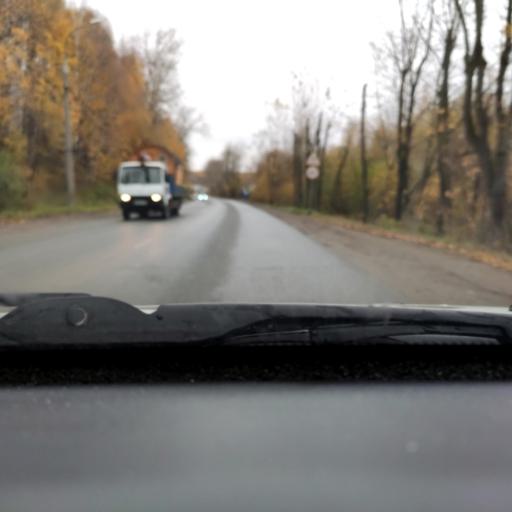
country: RU
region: Perm
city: Perm
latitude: 58.0793
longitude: 56.3498
